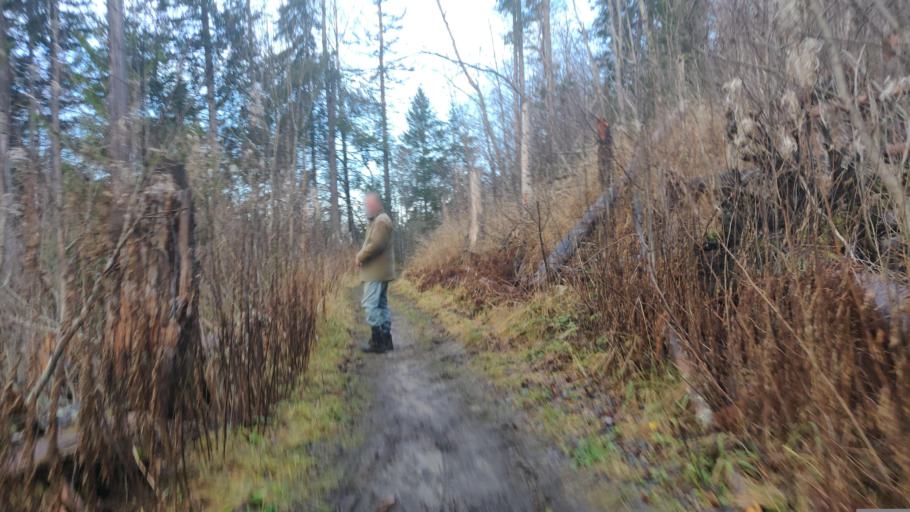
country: SE
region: Vaesternorrland
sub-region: Sundsvalls Kommun
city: Nolby
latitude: 62.3019
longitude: 17.3563
